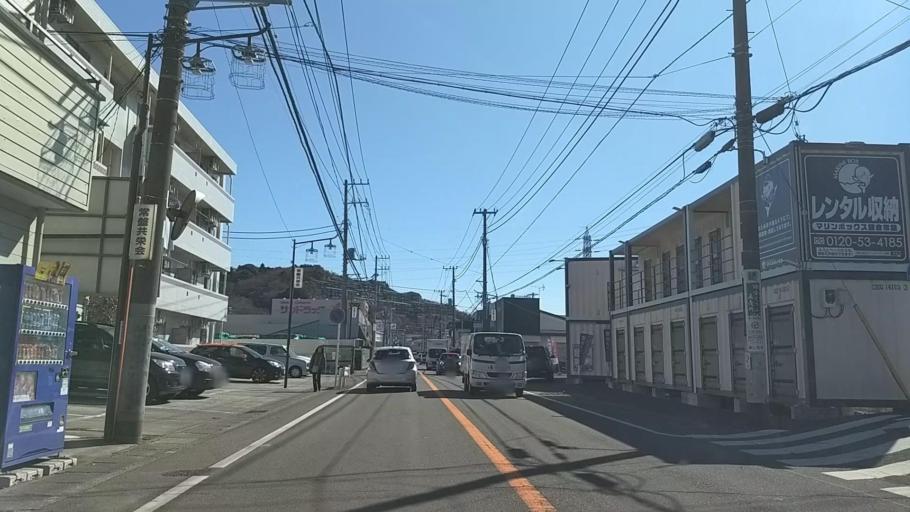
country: JP
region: Kanagawa
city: Kamakura
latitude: 35.3286
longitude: 139.5220
